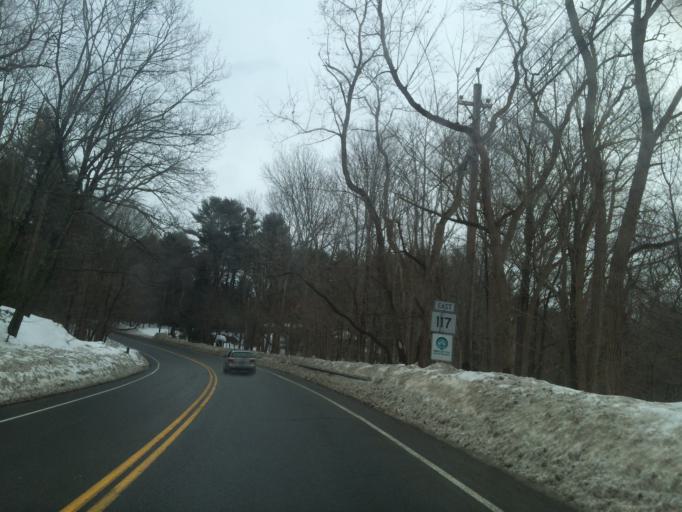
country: US
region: Massachusetts
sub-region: Middlesex County
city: Lincoln
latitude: 42.3987
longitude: -71.3062
